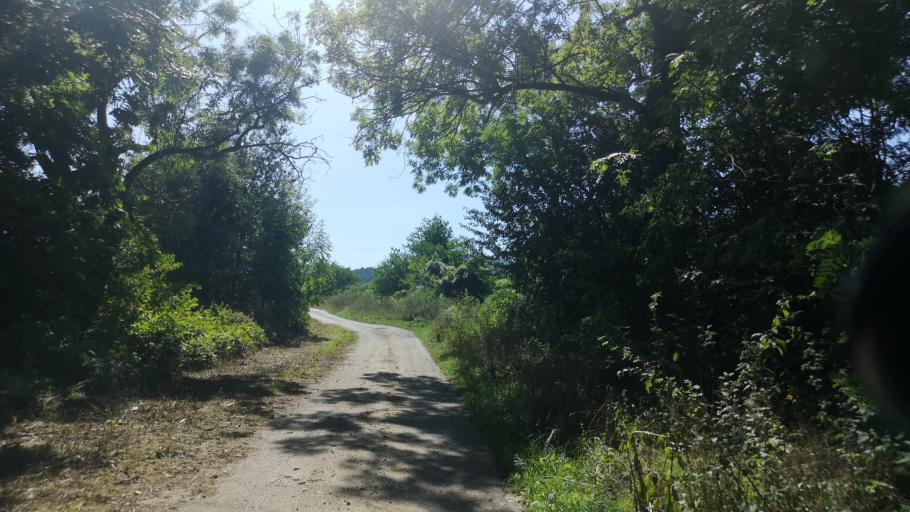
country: SK
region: Trnavsky
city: Smolenice
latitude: 48.5894
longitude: 17.4274
